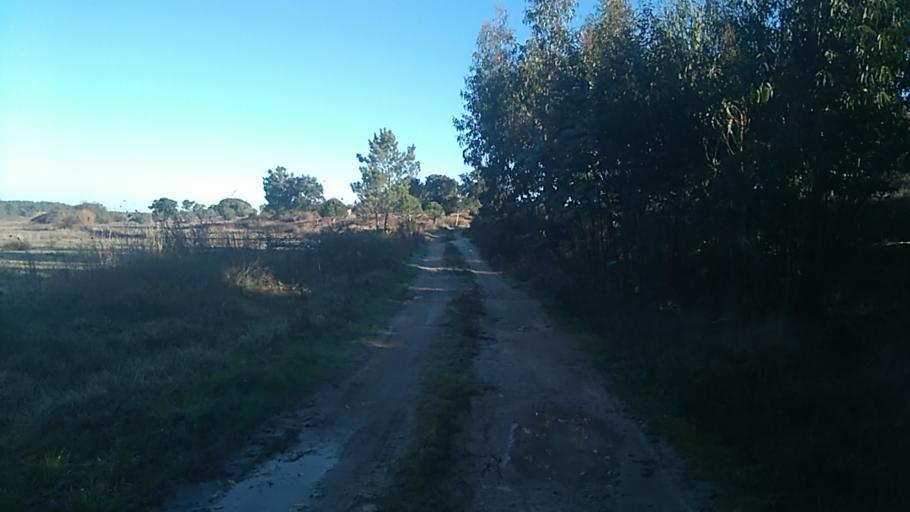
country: PT
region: Santarem
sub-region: Coruche
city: Coruche
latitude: 38.8653
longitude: -8.5185
